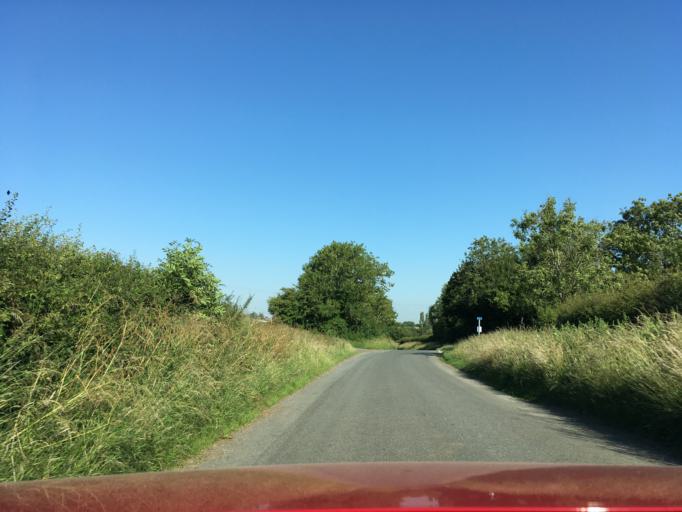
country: GB
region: England
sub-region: South Gloucestershire
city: Hinton
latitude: 51.4867
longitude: -2.3903
